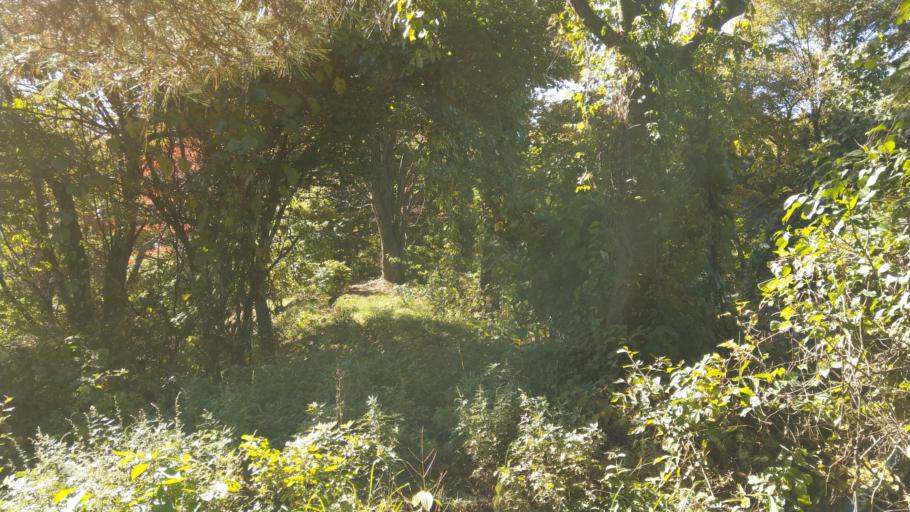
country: JP
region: Nagano
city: Komoro
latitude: 36.3559
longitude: 138.4336
